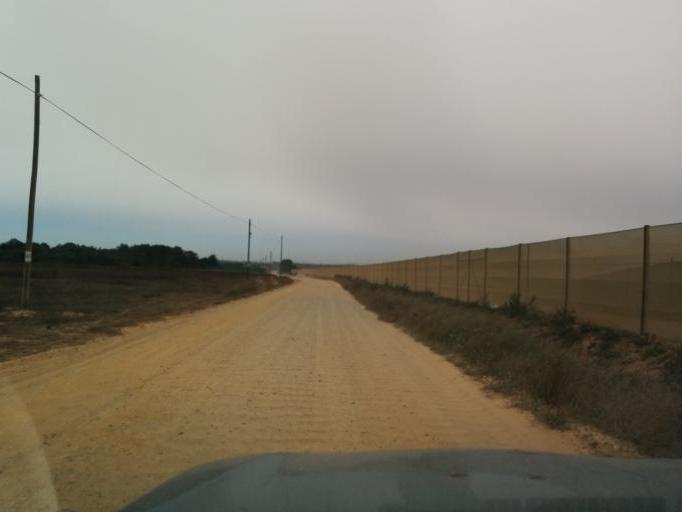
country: PT
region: Beja
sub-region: Odemira
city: Sao Teotonio
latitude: 37.5104
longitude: -8.7843
